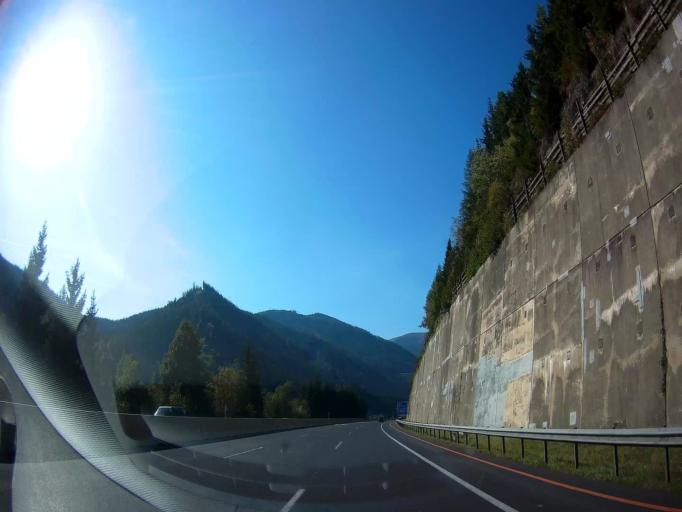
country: AT
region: Styria
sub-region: Politischer Bezirk Graz-Umgebung
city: Ubelbach
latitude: 47.2474
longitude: 15.1715
